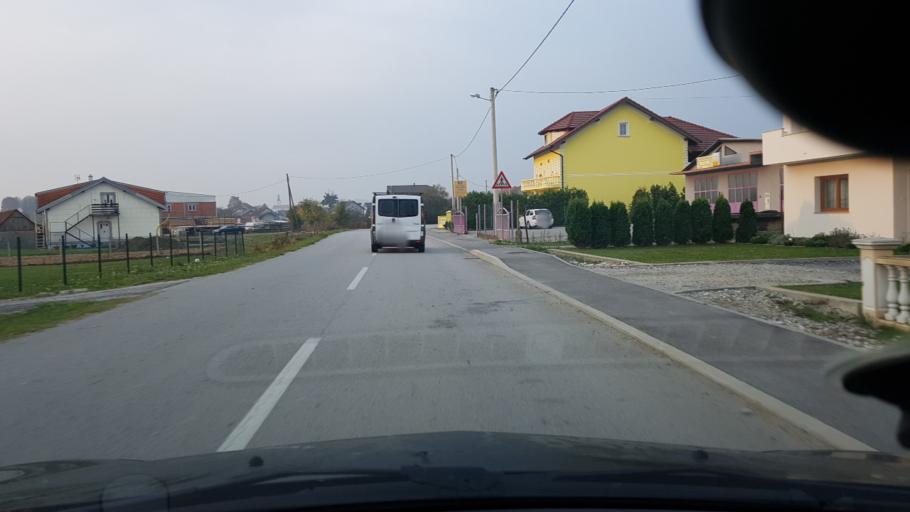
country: HR
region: Krapinsko-Zagorska
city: Zabok
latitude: 46.0898
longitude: 15.9057
